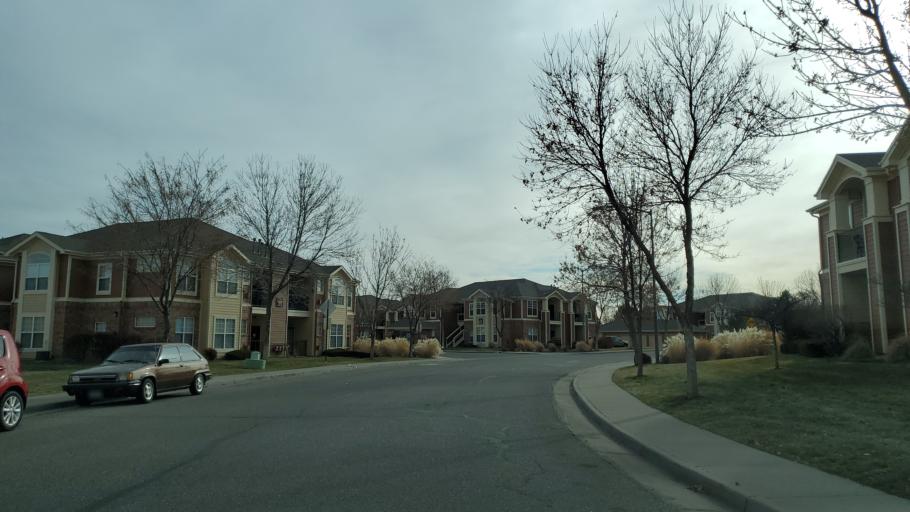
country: US
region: Colorado
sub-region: Adams County
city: Northglenn
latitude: 39.9155
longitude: -104.9463
